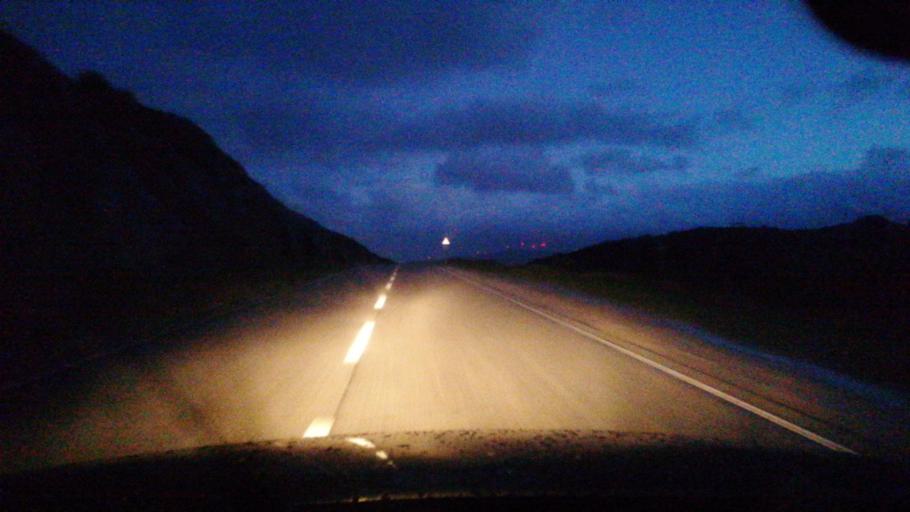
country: PT
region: Viseu
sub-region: Tabuaco
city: Tabuaco
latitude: 41.1356
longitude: -7.5214
